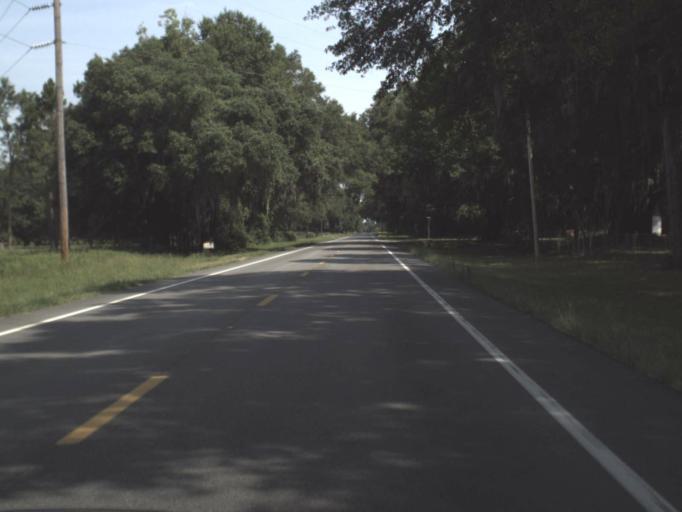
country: US
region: Florida
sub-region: Hamilton County
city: Jasper
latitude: 30.5534
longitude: -82.9806
